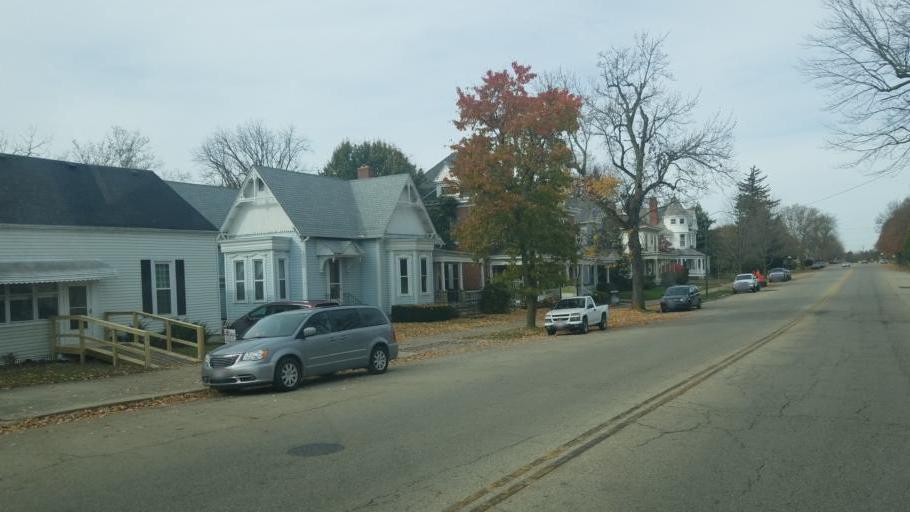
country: US
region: Ohio
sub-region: Madison County
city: London
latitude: 39.8881
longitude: -83.4506
